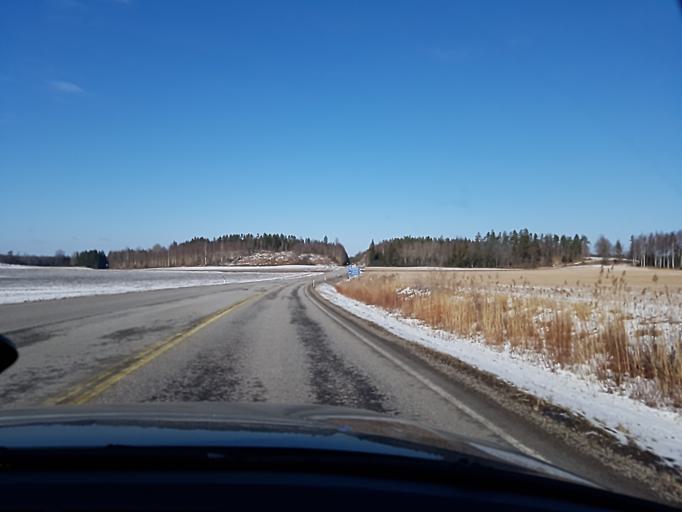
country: FI
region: Uusimaa
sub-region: Helsinki
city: Karjalohja
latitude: 60.1362
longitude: 23.8469
